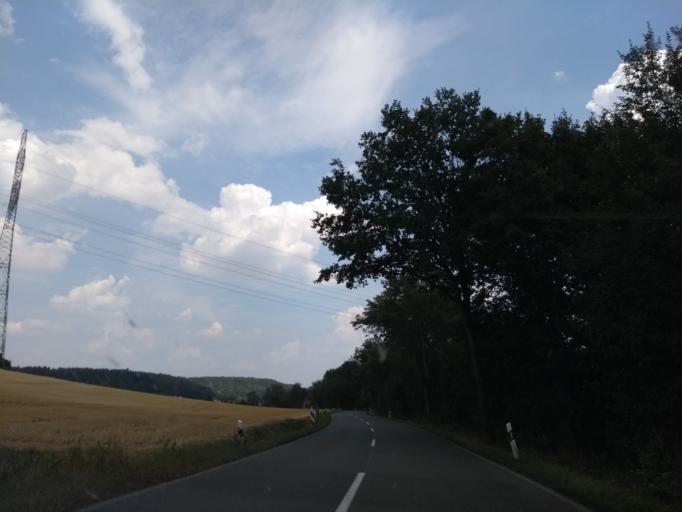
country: DE
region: Saxony-Anhalt
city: Wetterzeube
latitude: 51.0190
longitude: 12.0374
